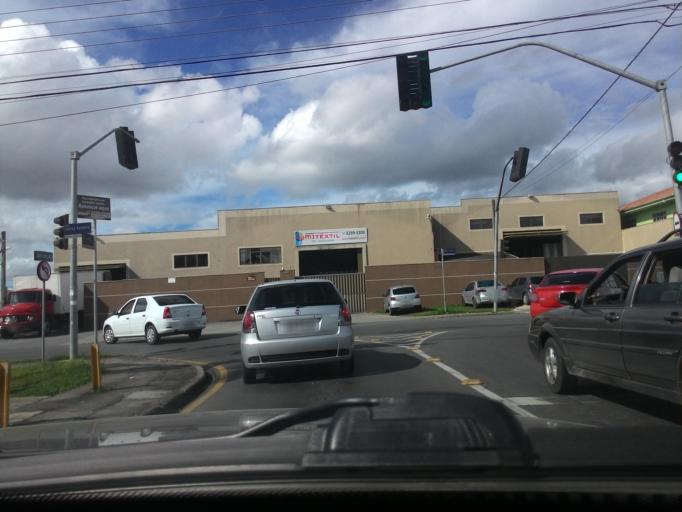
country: BR
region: Parana
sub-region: Sao Jose Dos Pinhais
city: Sao Jose dos Pinhais
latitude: -25.5189
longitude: -49.1901
